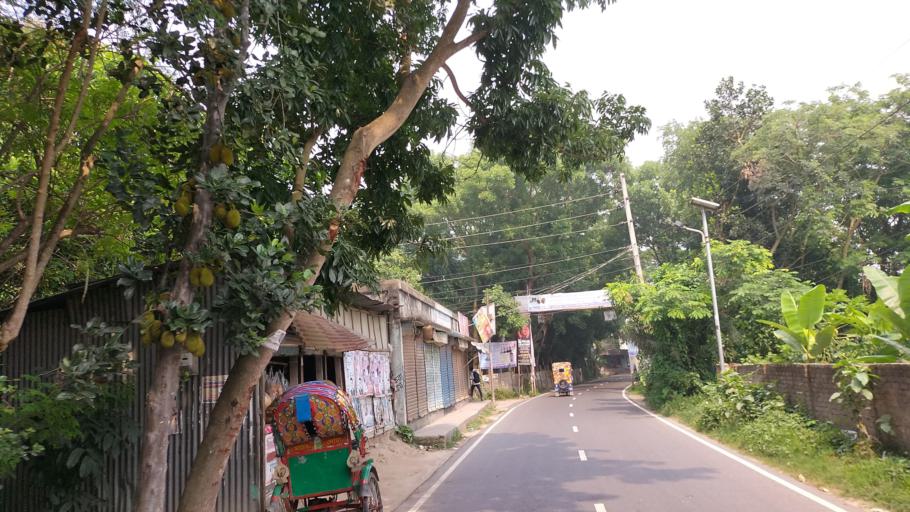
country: BD
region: Dhaka
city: Azimpur
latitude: 23.6960
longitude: 90.2981
